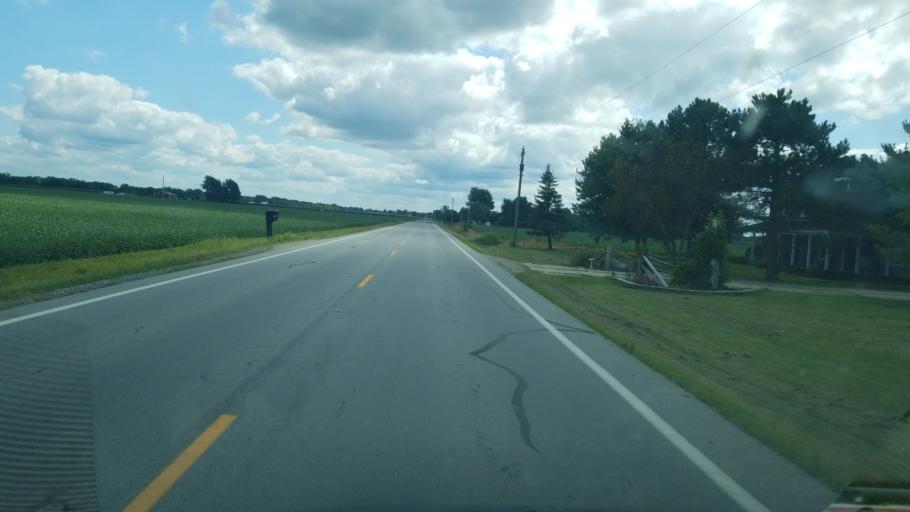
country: US
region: Ohio
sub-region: Allen County
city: Elida
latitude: 40.8479
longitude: -84.1379
